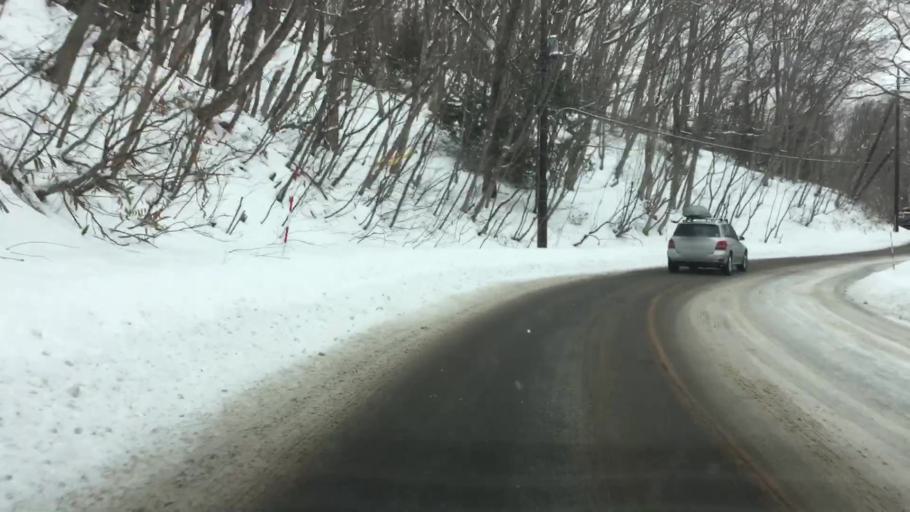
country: JP
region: Tochigi
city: Yaita
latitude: 36.9666
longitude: 139.7878
